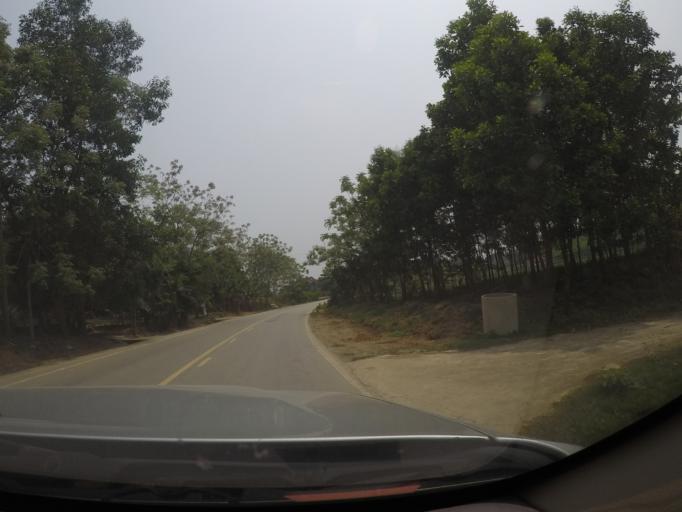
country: VN
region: Thanh Hoa
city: Thi Tran Yen Cat
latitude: 19.7042
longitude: 105.4507
